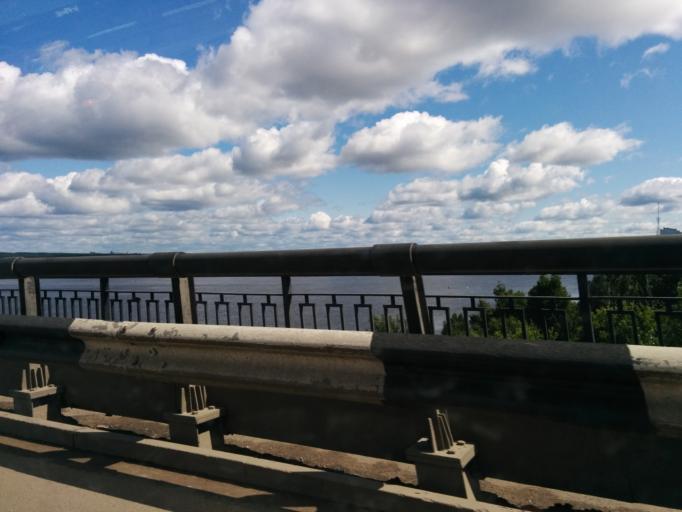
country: RU
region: Perm
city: Perm
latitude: 58.0159
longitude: 56.2232
